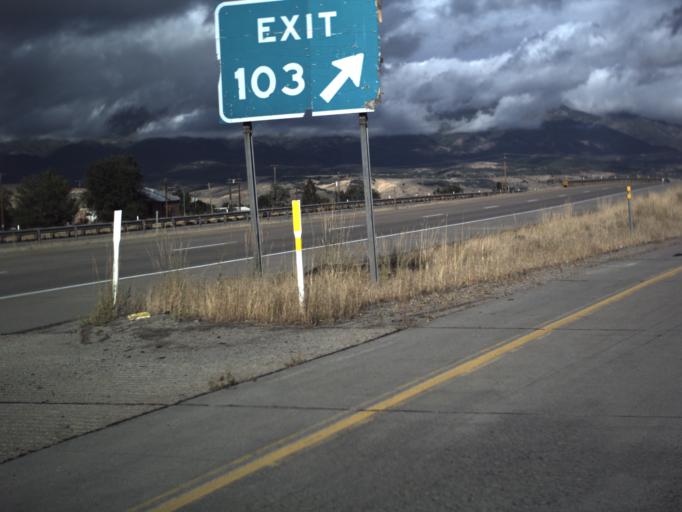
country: US
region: Utah
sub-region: Morgan County
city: Morgan
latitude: 41.0455
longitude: -111.6715
